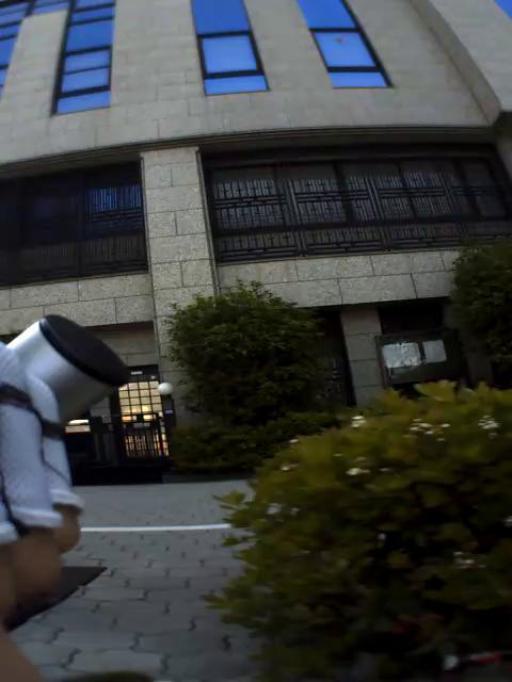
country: JP
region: Osaka
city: Osaka-shi
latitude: 34.6691
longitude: 135.5162
